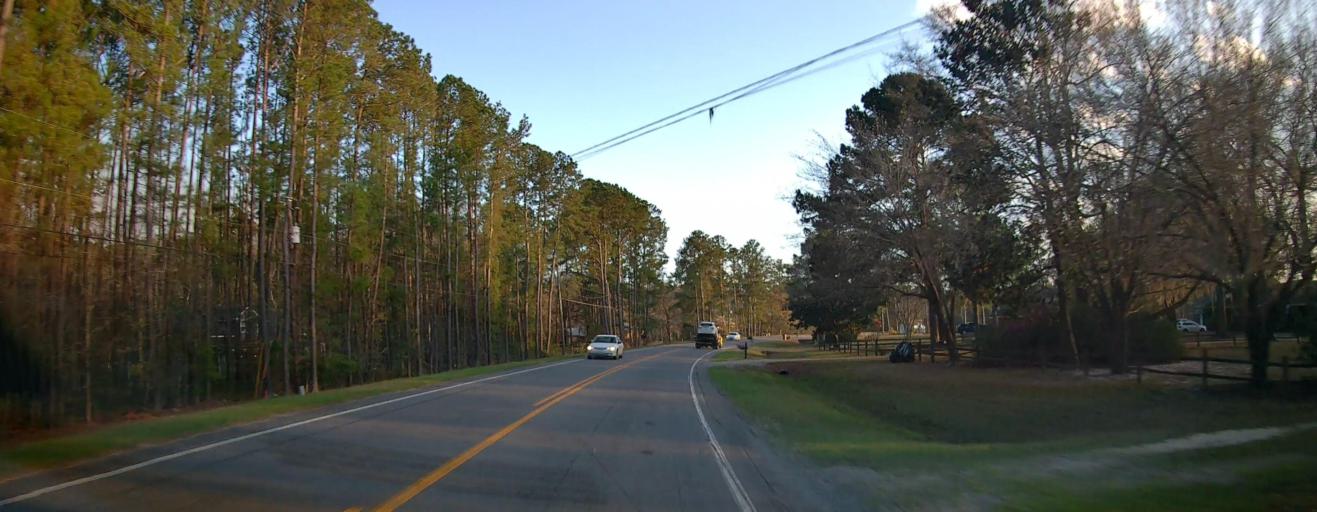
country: US
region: Georgia
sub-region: Chatham County
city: Bloomingdale
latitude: 32.1658
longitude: -81.3851
